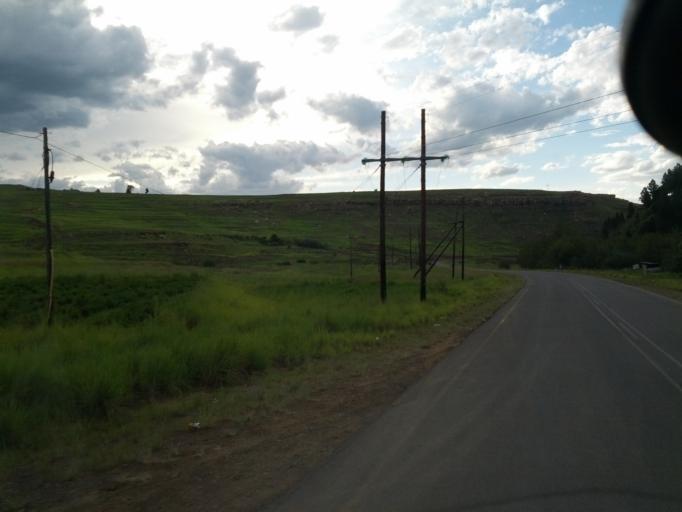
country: LS
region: Qacha's Nek
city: Qacha's Nek
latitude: -30.1066
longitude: 28.6626
